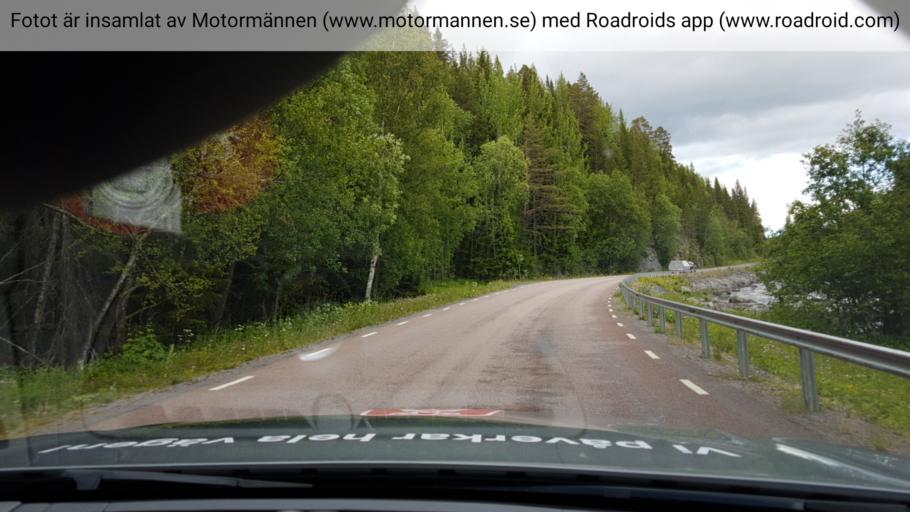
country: SE
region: Jaemtland
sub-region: Are Kommun
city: Jarpen
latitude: 63.1066
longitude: 13.8490
